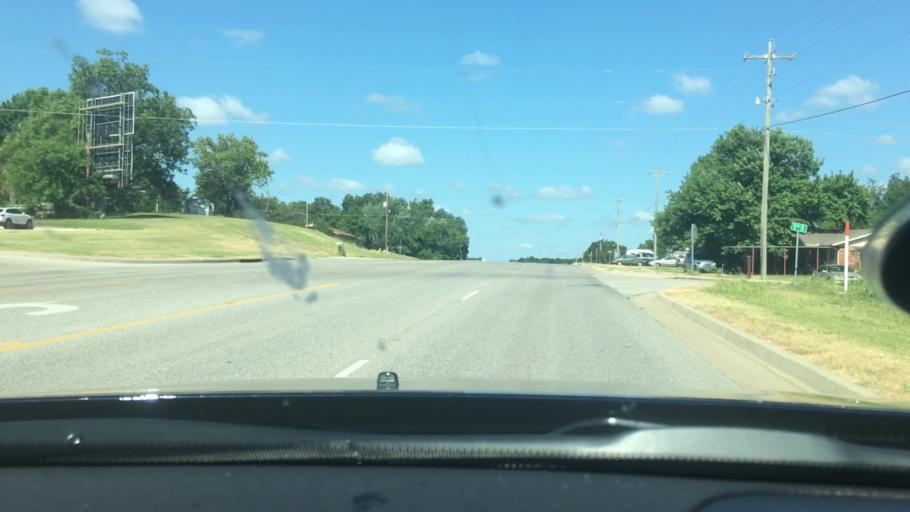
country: US
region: Oklahoma
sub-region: Marshall County
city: Oakland
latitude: 34.1001
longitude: -96.7971
